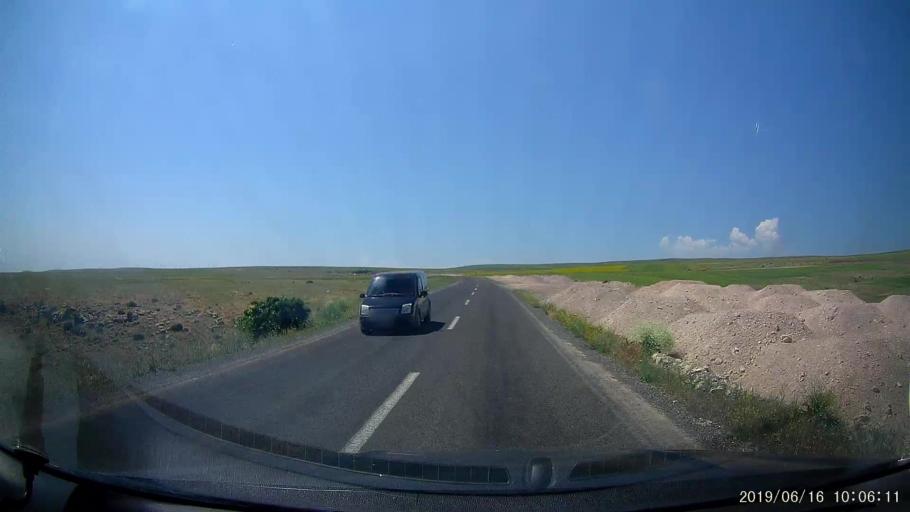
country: TR
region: Kars
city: Digor
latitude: 40.2589
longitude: 43.5411
